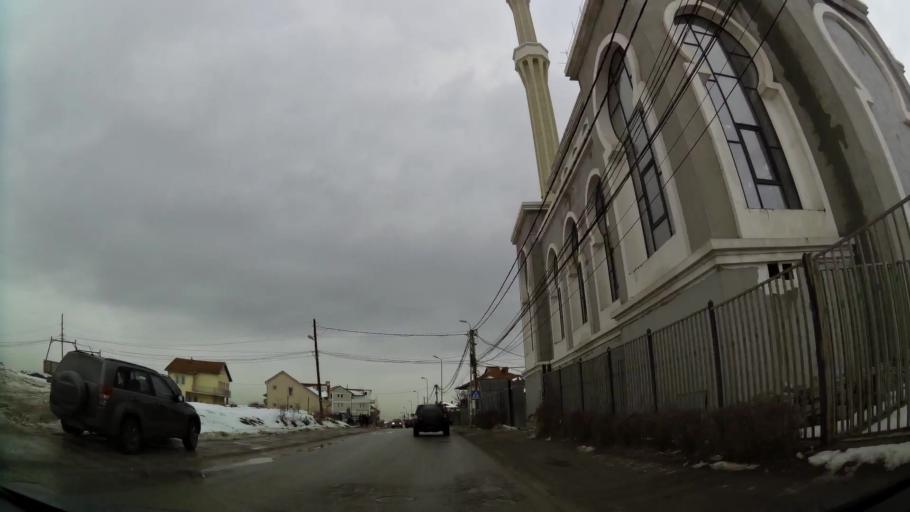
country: XK
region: Pristina
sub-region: Komuna e Prishtines
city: Pristina
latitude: 42.6565
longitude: 21.1877
